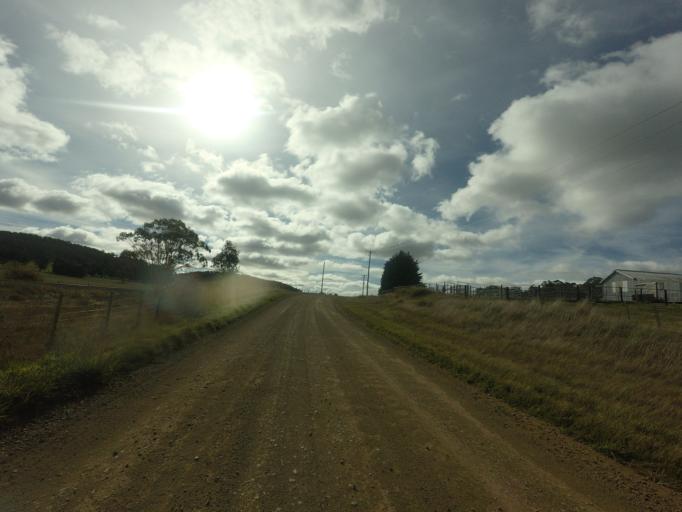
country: AU
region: Tasmania
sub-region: Brighton
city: Bridgewater
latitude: -42.3998
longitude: 147.3911
